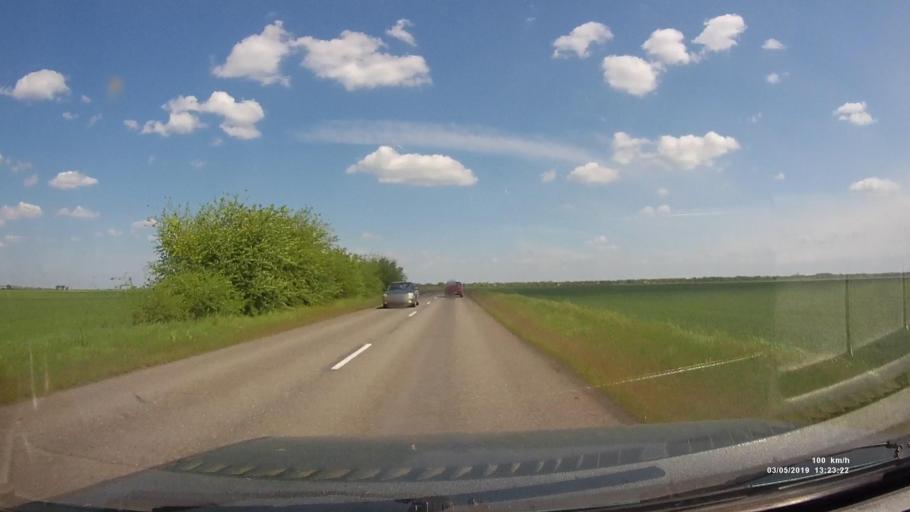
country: RU
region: Rostov
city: Semikarakorsk
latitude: 47.5627
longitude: 40.7801
